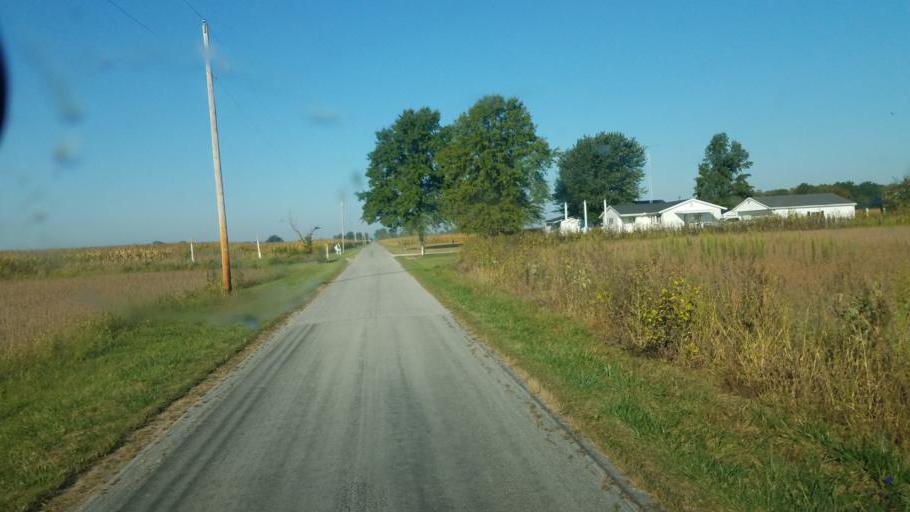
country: US
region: Ohio
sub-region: Union County
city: Richwood
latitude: 40.5514
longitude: -83.2824
